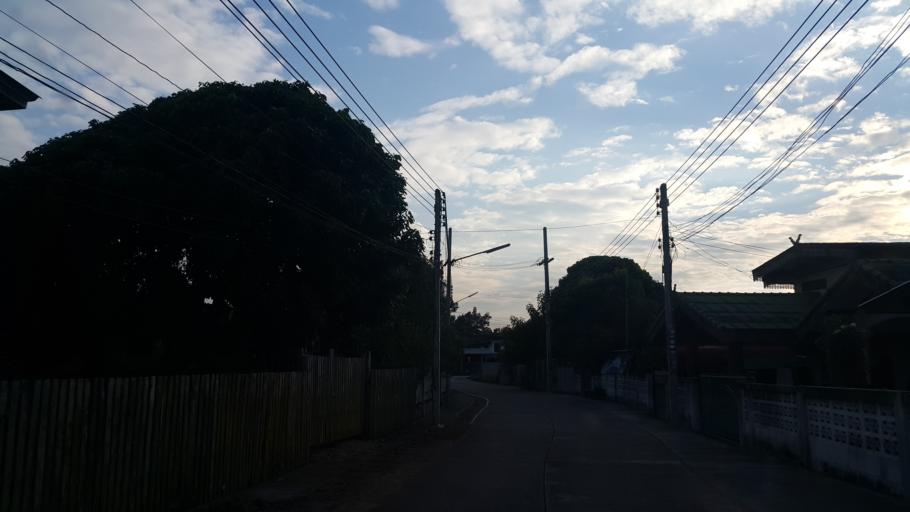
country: TH
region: Lampang
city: Sop Prap
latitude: 17.8885
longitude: 99.3354
